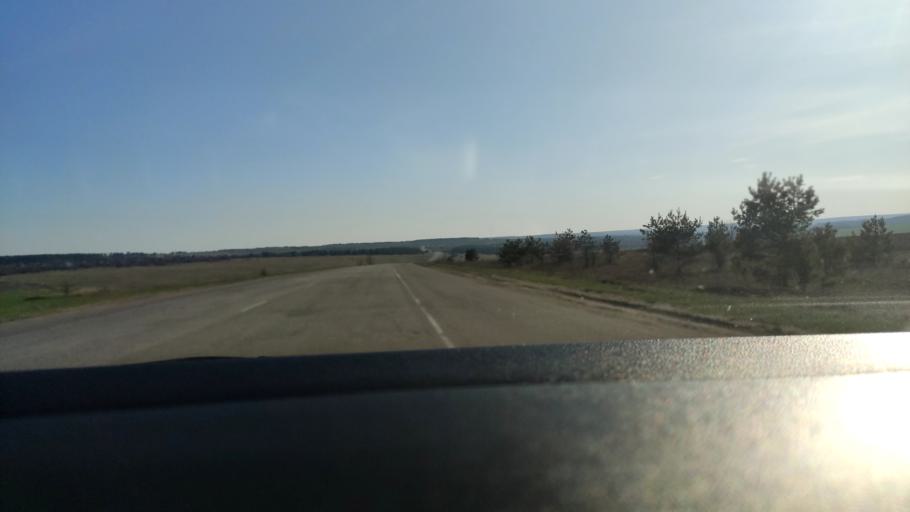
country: RU
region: Voronezj
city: Kolodeznyy
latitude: 51.3923
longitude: 39.2305
